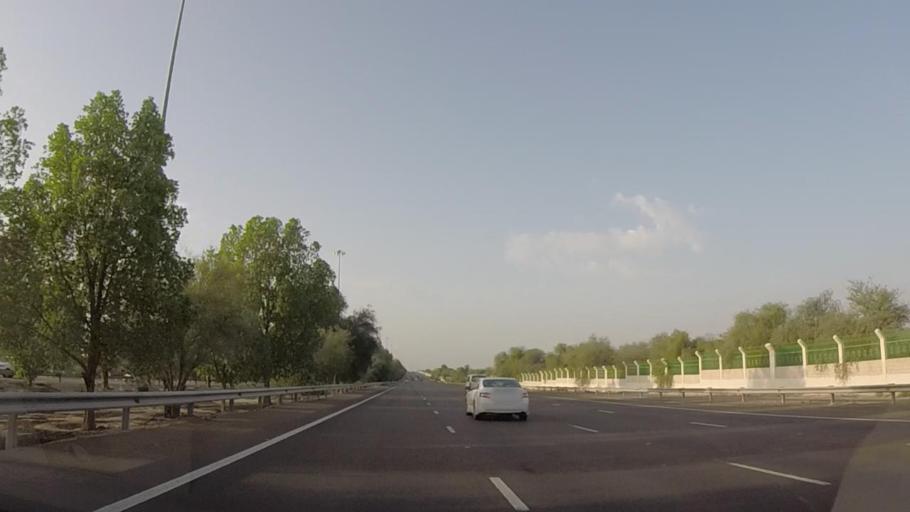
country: AE
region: Dubai
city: Dubai
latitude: 24.7658
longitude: 54.8462
